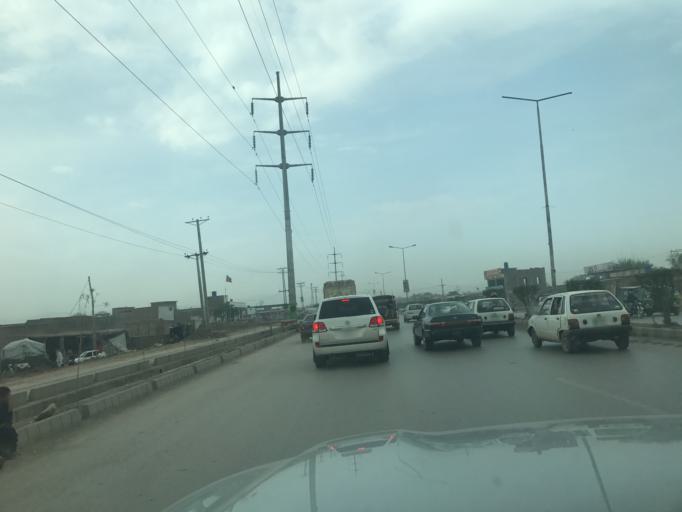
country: PK
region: Khyber Pakhtunkhwa
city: Peshawar
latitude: 33.9729
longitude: 71.5448
